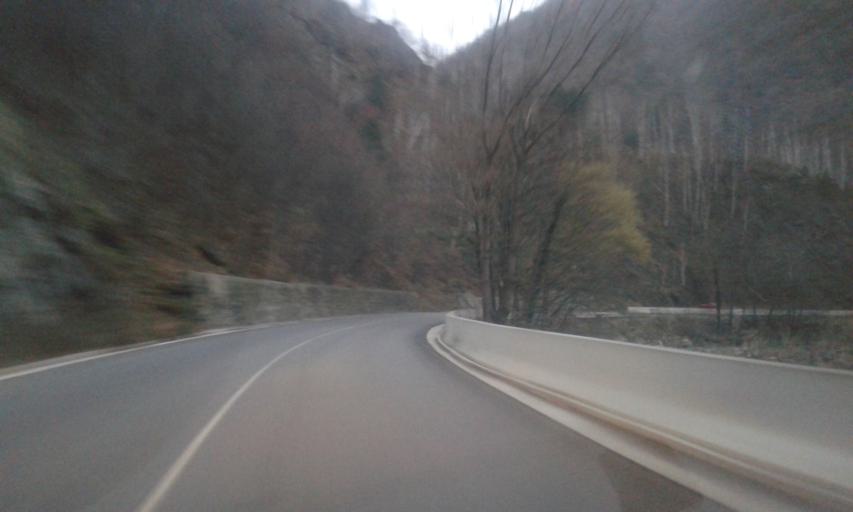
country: RO
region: Gorj
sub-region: Comuna Bumbesti-Jiu
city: Bumbesti-Jiu
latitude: 45.2026
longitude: 23.3786
